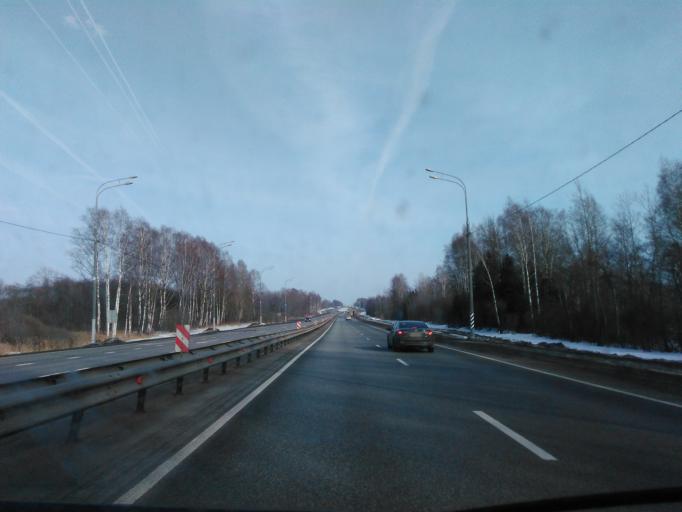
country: RU
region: Smolensk
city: Safonovo
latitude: 55.1285
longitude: 33.1543
